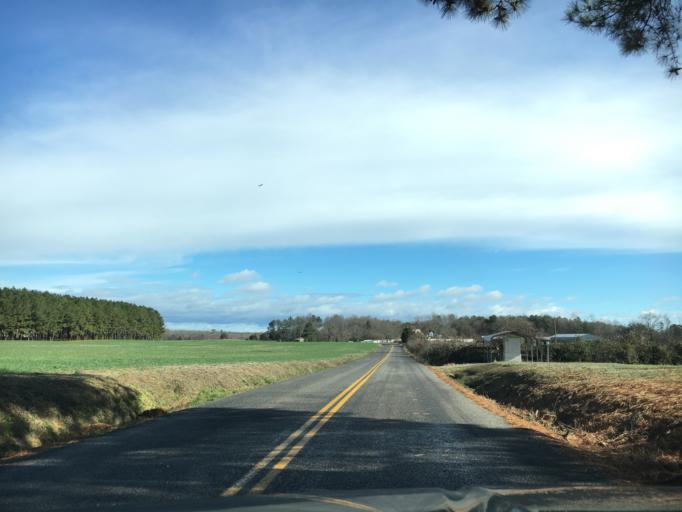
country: US
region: Virginia
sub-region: Amelia County
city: Amelia Court House
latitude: 37.4185
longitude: -78.0758
